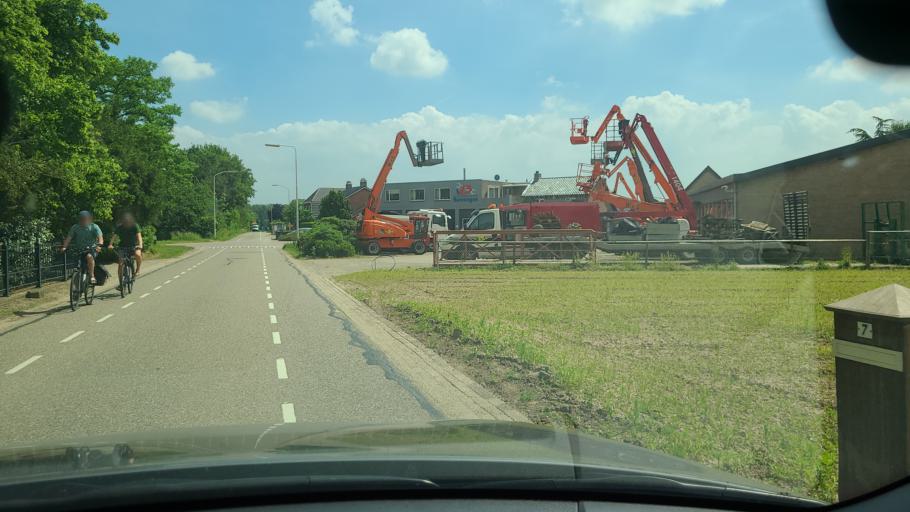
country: NL
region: Gelderland
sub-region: Gemeente Druten
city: Druten
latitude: 51.8670
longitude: 5.6127
